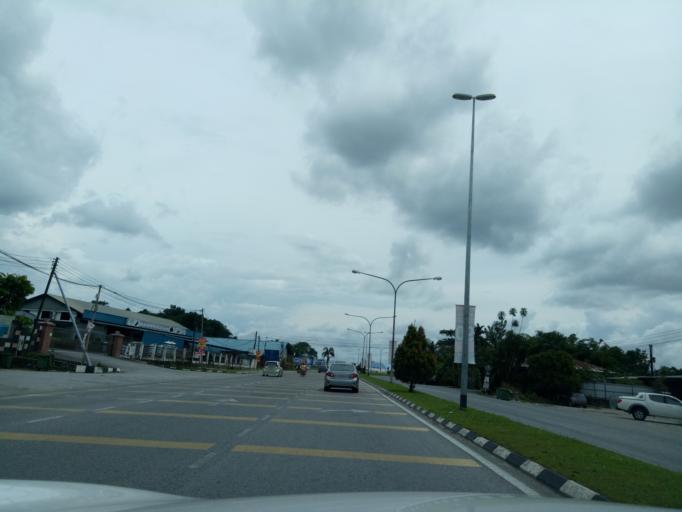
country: MY
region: Sarawak
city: Kuching
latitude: 1.4996
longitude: 110.3345
